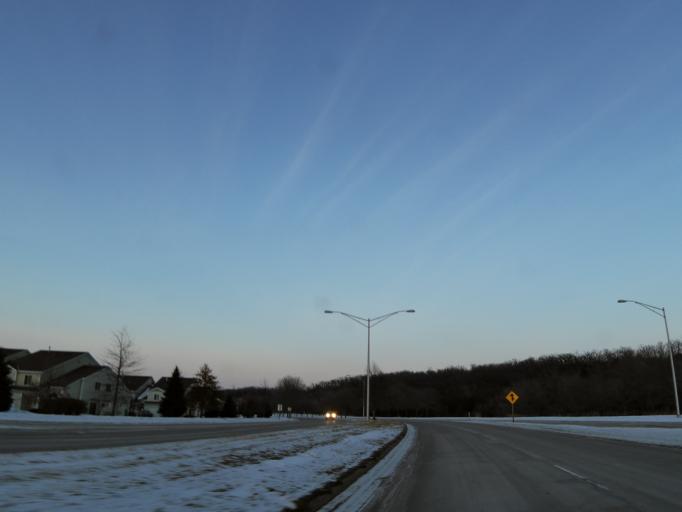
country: US
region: Wisconsin
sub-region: Saint Croix County
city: Hudson
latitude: 44.9487
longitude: -92.7238
